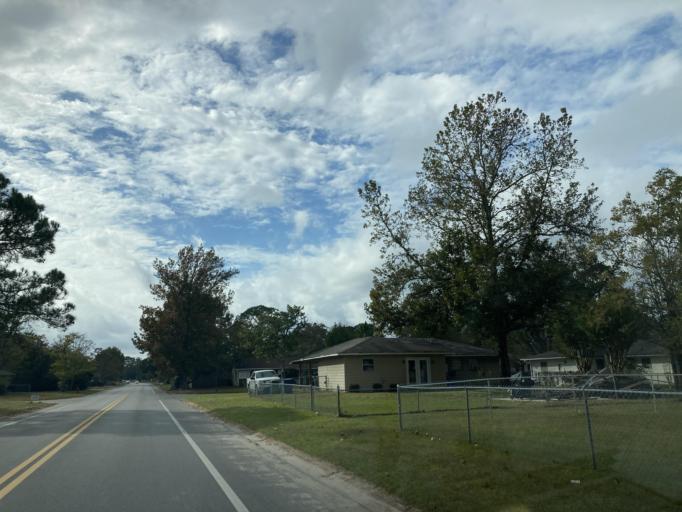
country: US
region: Mississippi
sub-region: Jackson County
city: Gulf Hills
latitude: 30.4360
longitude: -88.8248
